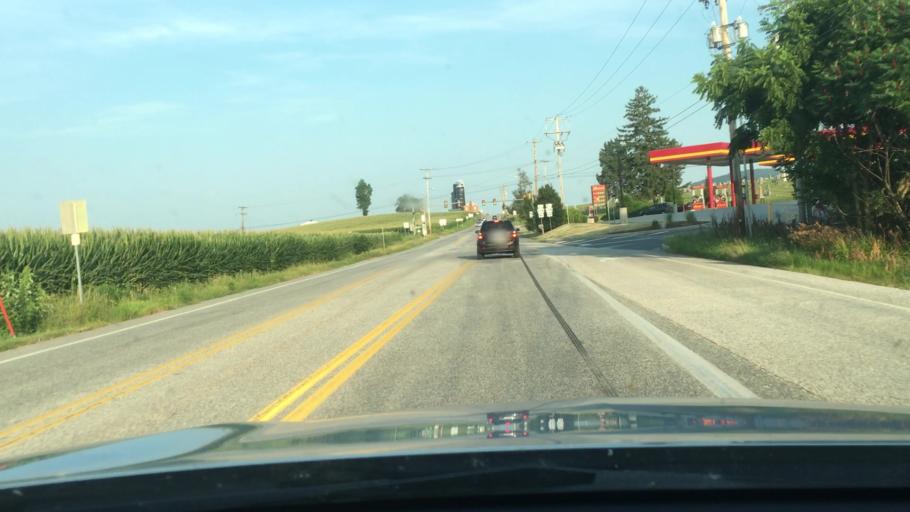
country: US
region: Pennsylvania
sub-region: Cumberland County
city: Boiling Springs
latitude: 40.1611
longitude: -77.0958
